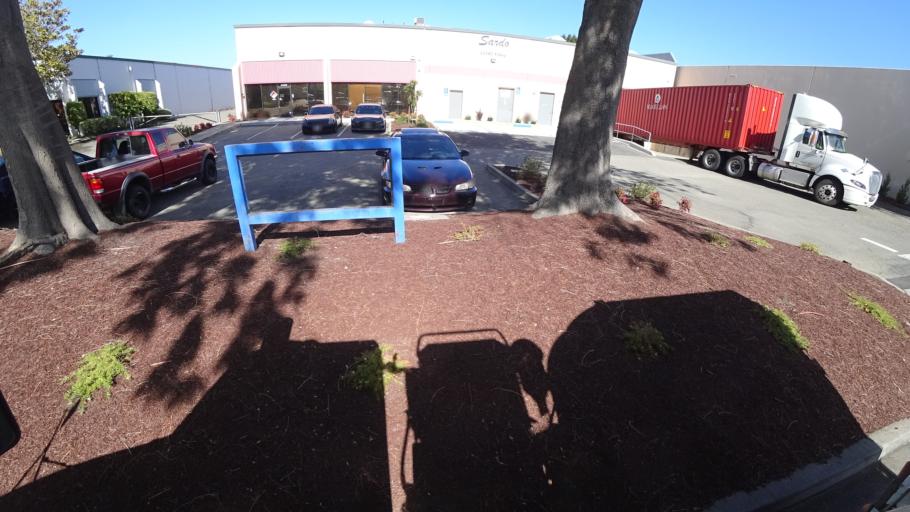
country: US
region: California
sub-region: Alameda County
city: San Lorenzo
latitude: 37.6421
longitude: -122.1315
